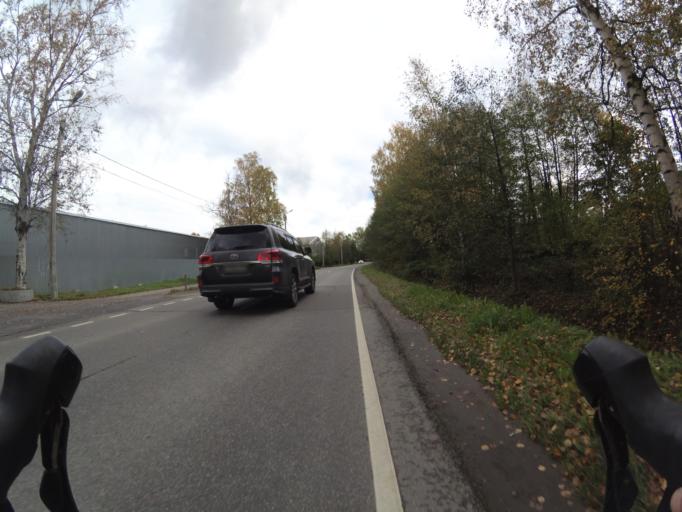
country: RU
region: St.-Petersburg
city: Lakhtinskiy
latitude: 59.9951
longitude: 30.1514
